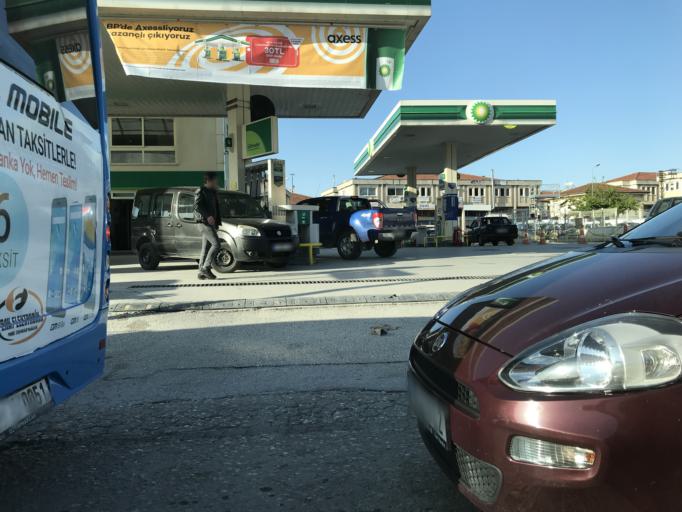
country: TR
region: Hatay
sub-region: Antakya Ilcesi
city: Antakya
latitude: 36.2088
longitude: 36.1656
